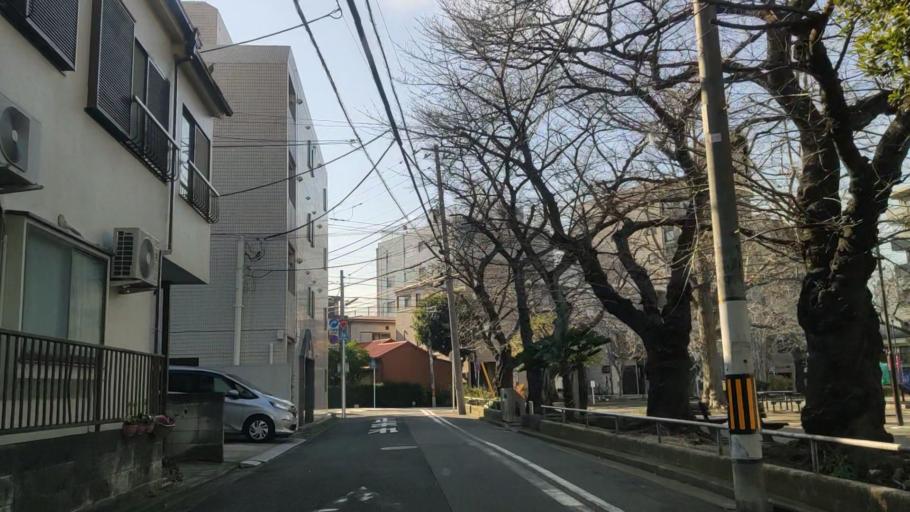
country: JP
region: Kanagawa
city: Yokohama
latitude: 35.4526
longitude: 139.6112
